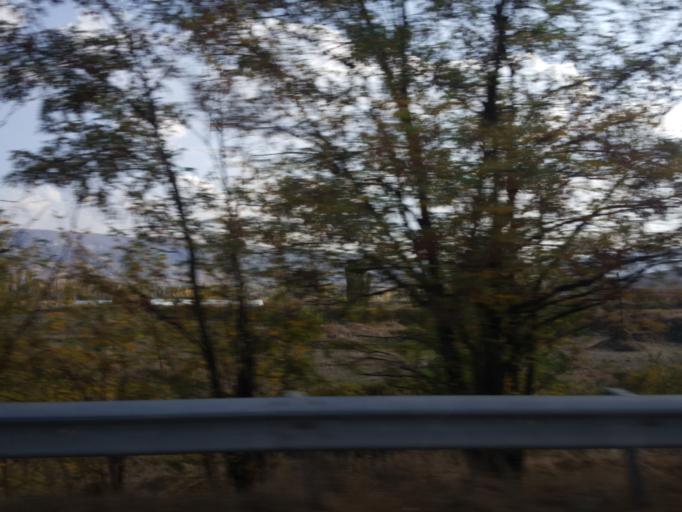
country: TR
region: Corum
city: Seydim
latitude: 40.4309
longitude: 34.7912
